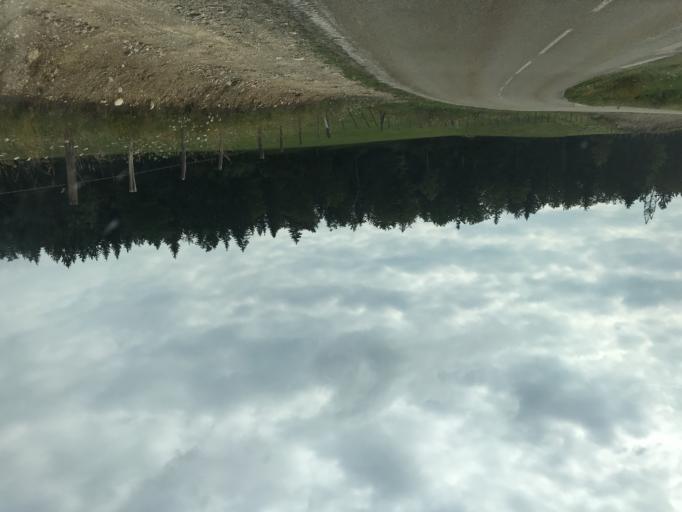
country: FR
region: Franche-Comte
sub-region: Departement du Jura
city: Longchaumois
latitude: 46.5064
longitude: 5.8937
